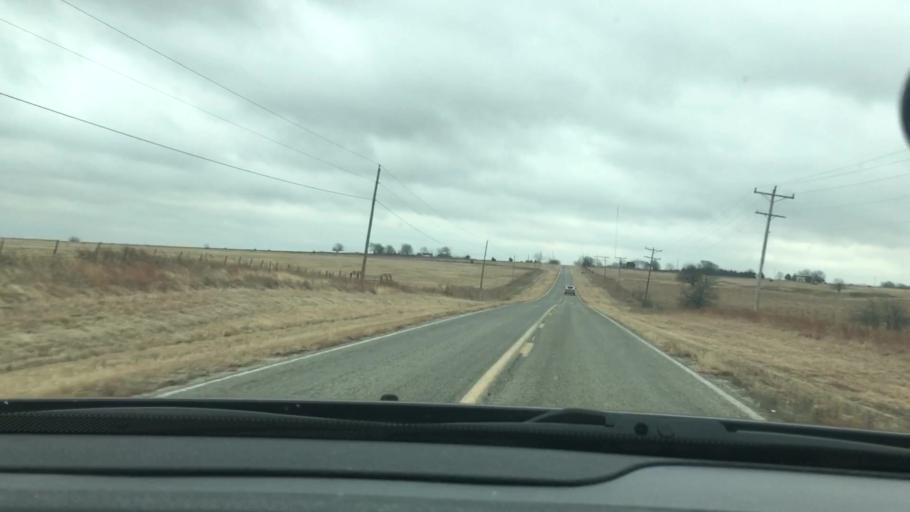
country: US
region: Oklahoma
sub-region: Johnston County
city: Tishomingo
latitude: 34.1433
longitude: -96.5116
